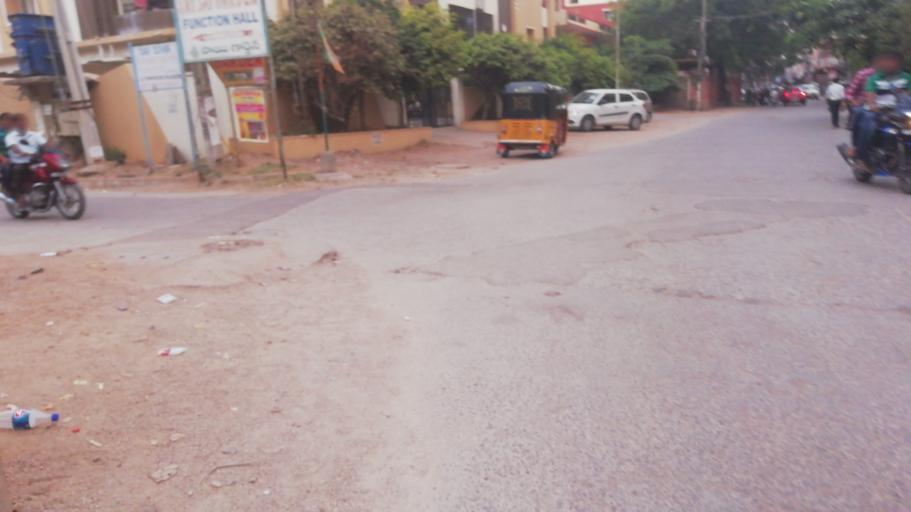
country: IN
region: Telangana
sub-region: Rangareddi
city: Gaddi Annaram
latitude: 17.3648
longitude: 78.5347
